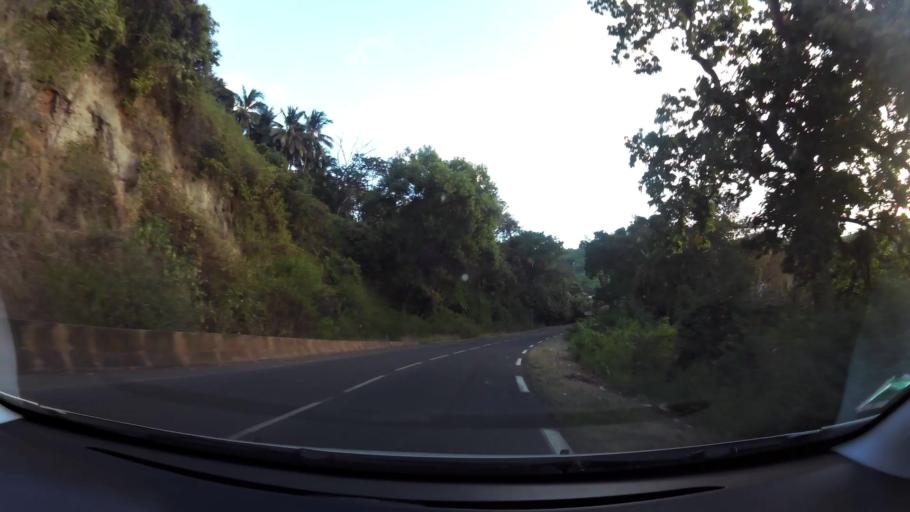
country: YT
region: Koungou
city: Koungou
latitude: -12.7297
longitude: 45.1892
